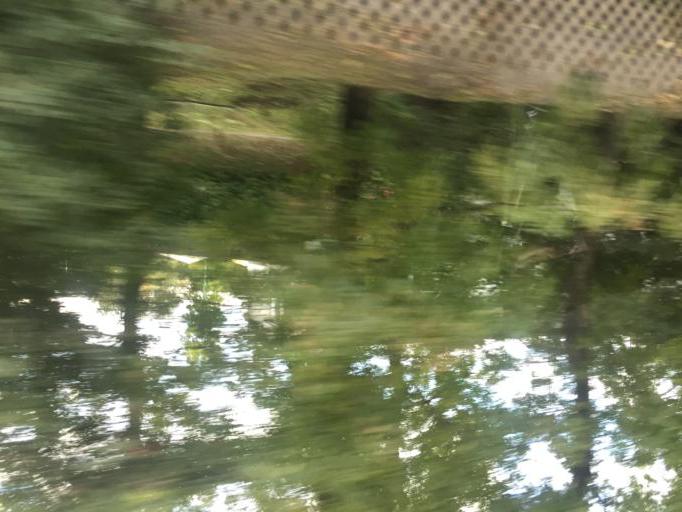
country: RU
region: Kaliningrad
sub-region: Gorod Kaliningrad
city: Kaliningrad
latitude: 54.7421
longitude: 20.4725
